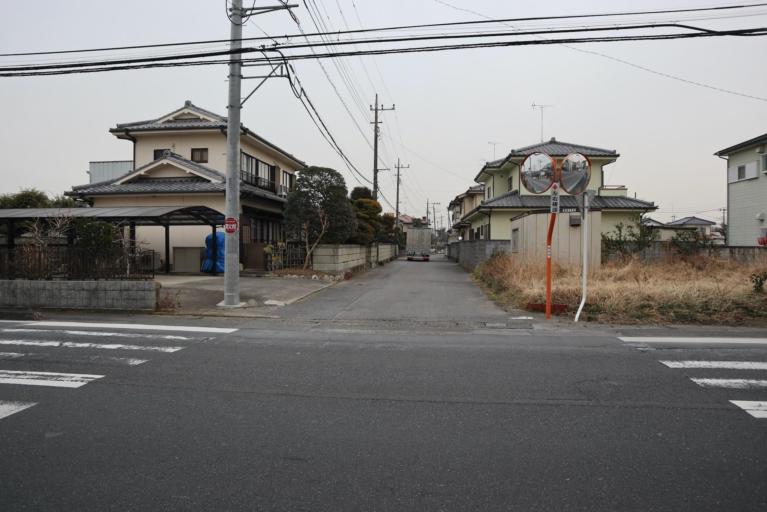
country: JP
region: Saitama
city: Hanyu
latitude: 36.1795
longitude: 139.5049
